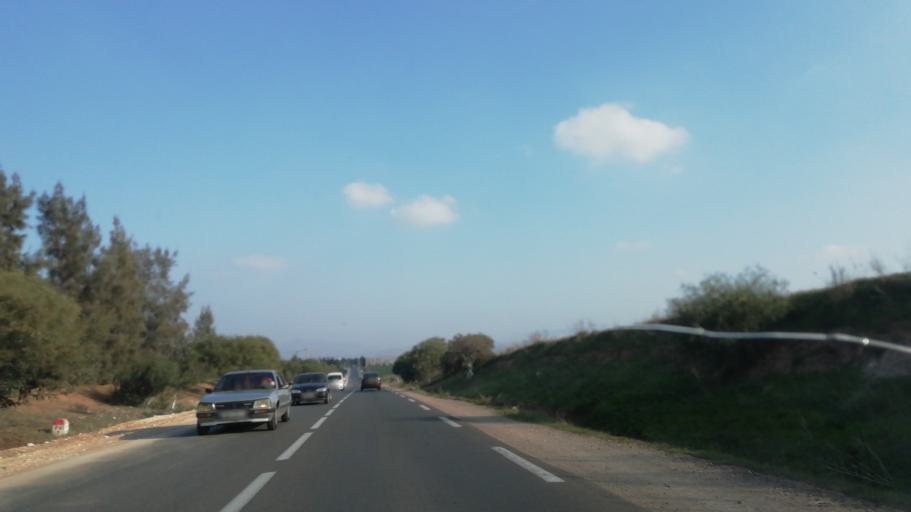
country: DZ
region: Ain Temouchent
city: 'Ain Temouchent
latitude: 35.3041
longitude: -1.0406
